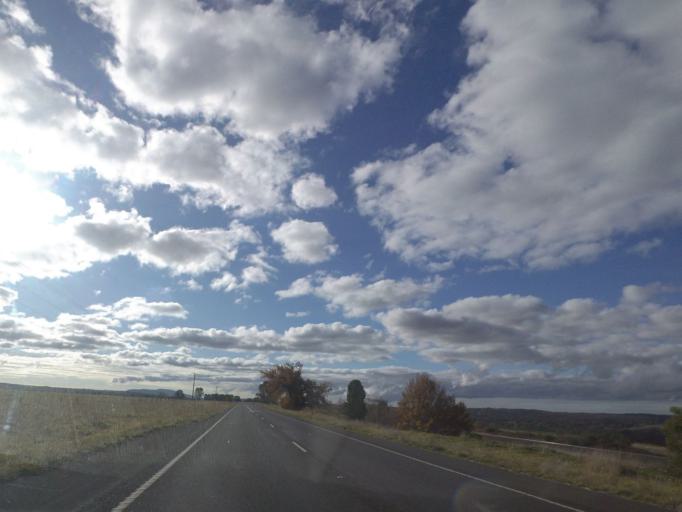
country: AU
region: Victoria
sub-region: Mount Alexander
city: Castlemaine
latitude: -37.1666
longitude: 144.3580
